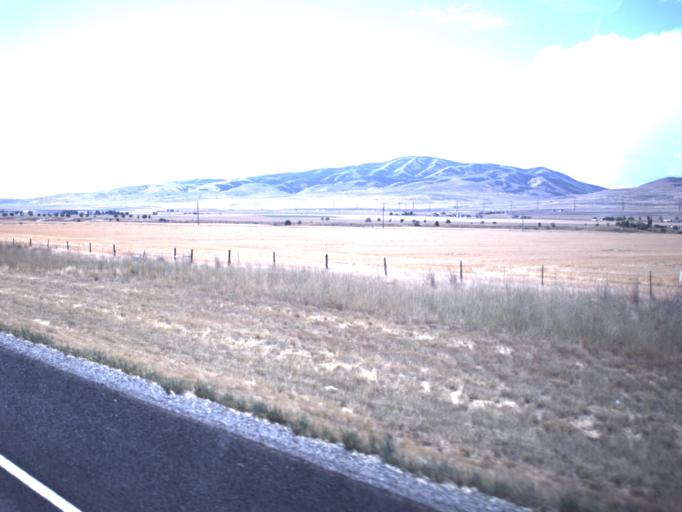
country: US
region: Utah
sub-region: Box Elder County
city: Garland
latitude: 41.8609
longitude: -112.1466
